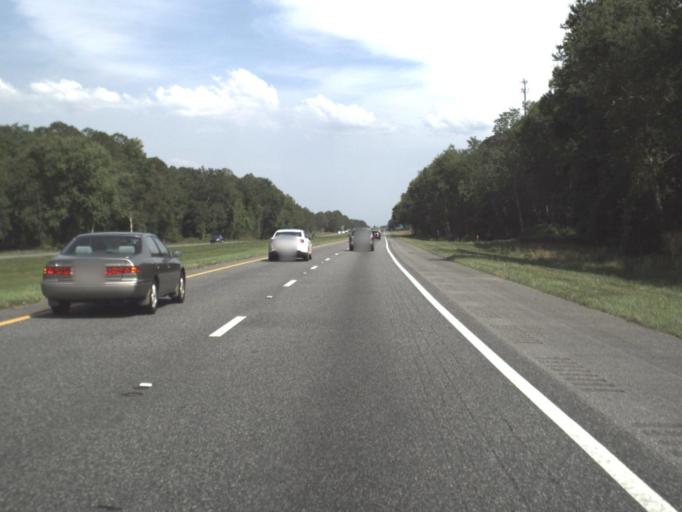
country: US
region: Florida
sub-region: Baker County
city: Macclenny
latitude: 30.2508
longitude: -82.3245
